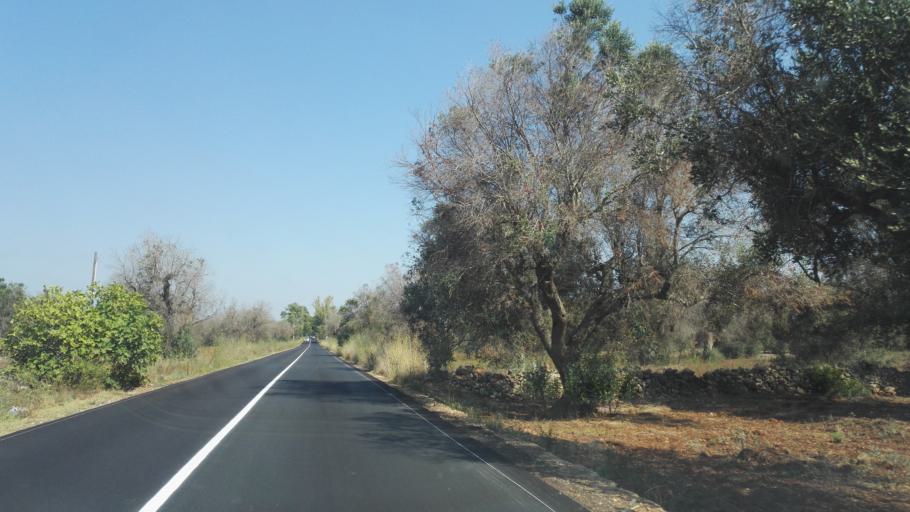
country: IT
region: Apulia
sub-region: Provincia di Lecce
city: Nardo
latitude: 40.1935
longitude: 17.9646
